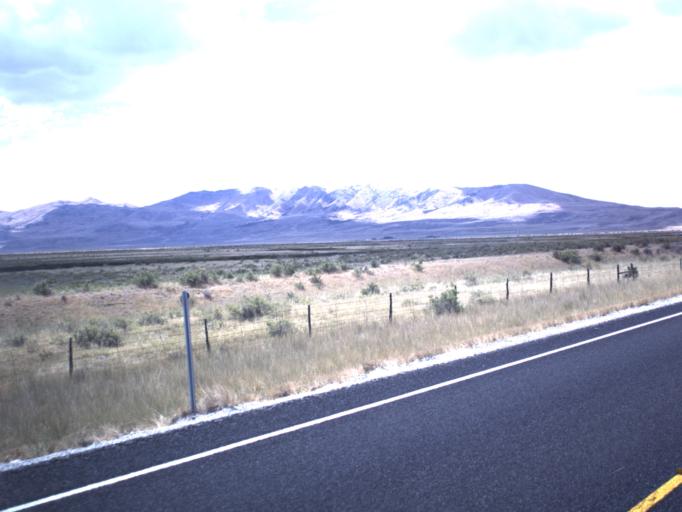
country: US
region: Utah
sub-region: Box Elder County
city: Tremonton
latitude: 41.6291
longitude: -112.4115
